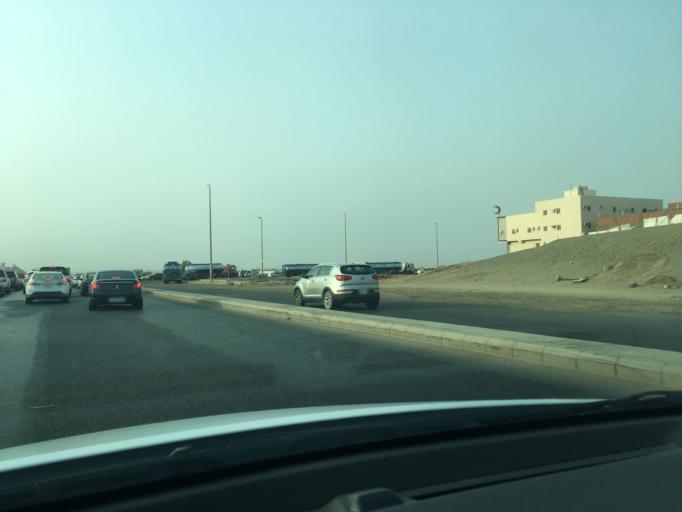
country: SA
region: Makkah
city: Jeddah
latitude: 21.7642
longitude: 39.1825
